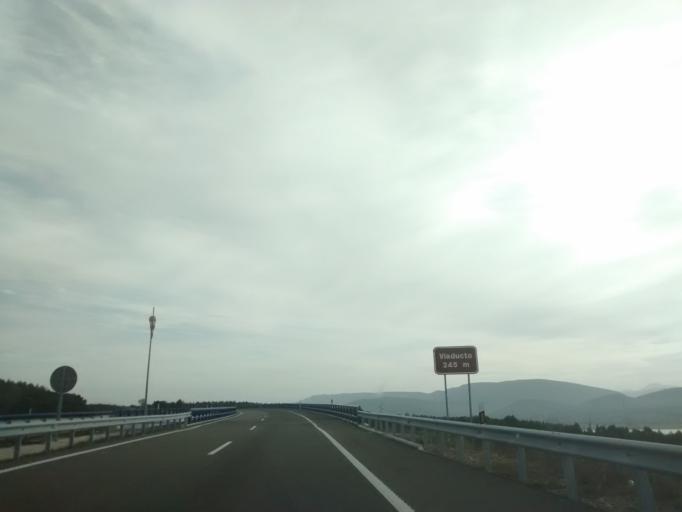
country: ES
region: Navarre
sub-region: Provincia de Navarra
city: Yesa
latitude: 42.6193
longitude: -1.1479
